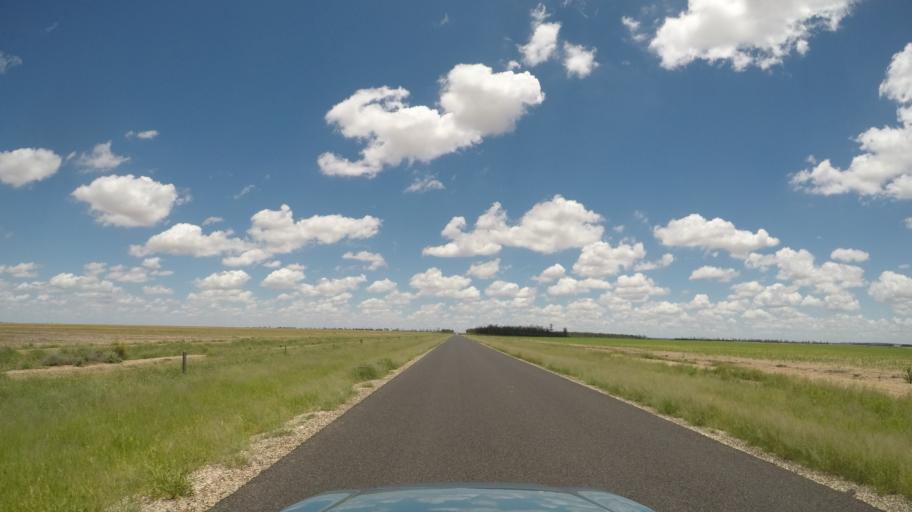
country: AU
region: Queensland
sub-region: Goondiwindi
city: Goondiwindi
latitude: -28.1748
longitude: 150.2479
